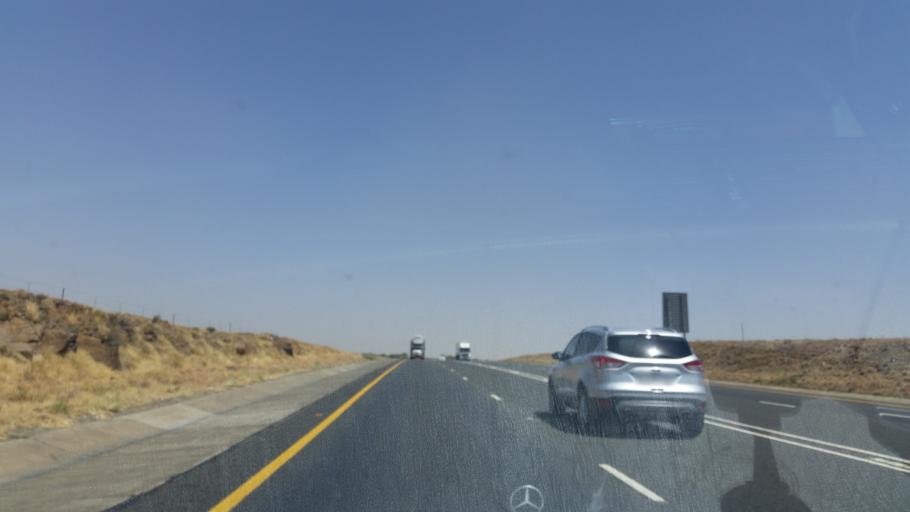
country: ZA
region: Orange Free State
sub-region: Lejweleputswa District Municipality
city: Winburg
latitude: -28.6907
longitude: 26.8144
